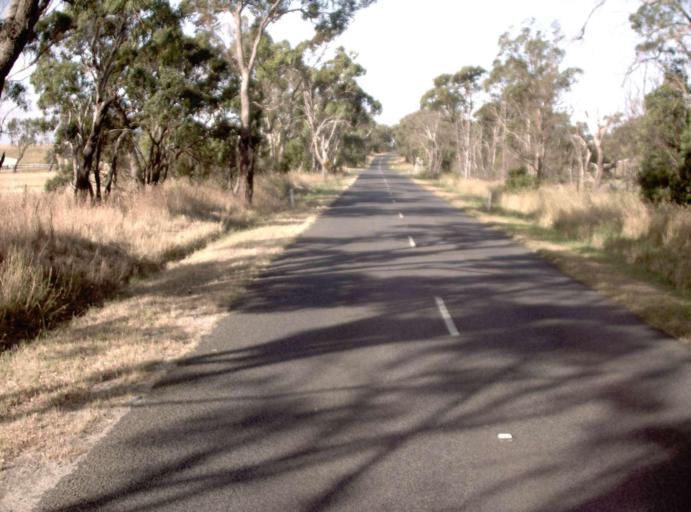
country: AU
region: Victoria
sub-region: Latrobe
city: Morwell
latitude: -38.2728
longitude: 146.4683
